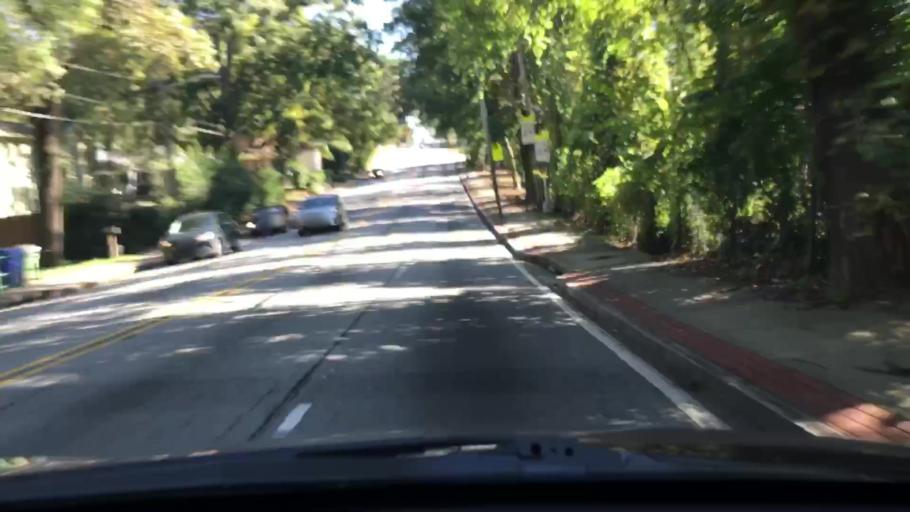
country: US
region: Georgia
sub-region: DeKalb County
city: Decatur
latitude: 33.7473
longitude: -84.3162
